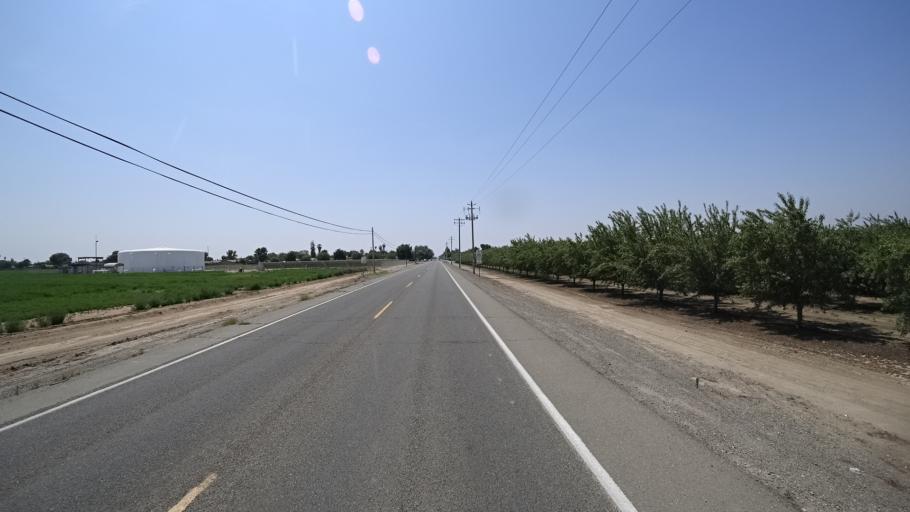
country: US
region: California
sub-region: Kings County
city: Lemoore
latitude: 36.3230
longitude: -119.7808
